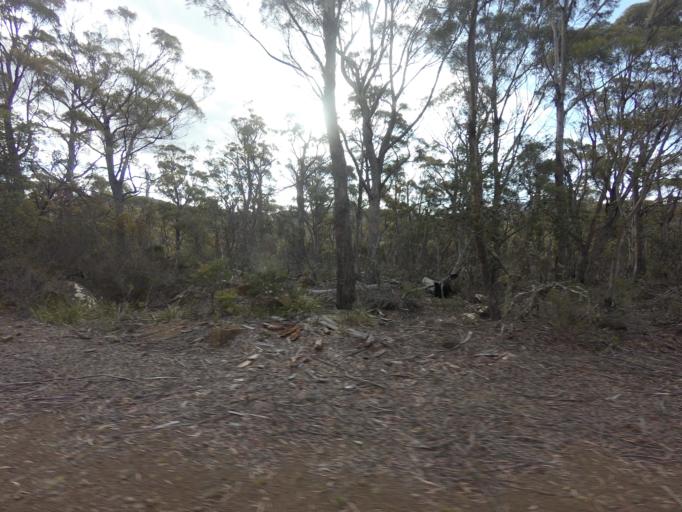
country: AU
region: Tasmania
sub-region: Break O'Day
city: St Helens
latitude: -41.8599
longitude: 148.0238
